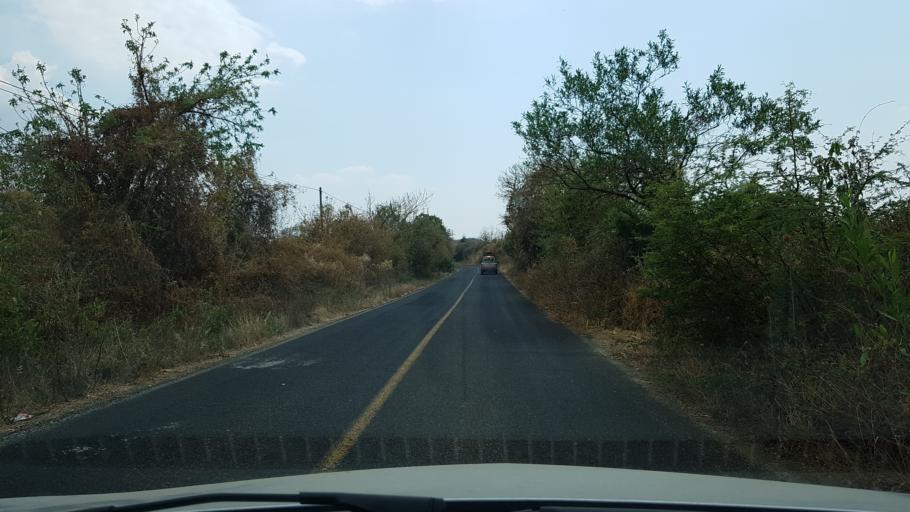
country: MX
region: Morelos
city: Tlacotepec
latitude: 18.8346
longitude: -98.7352
